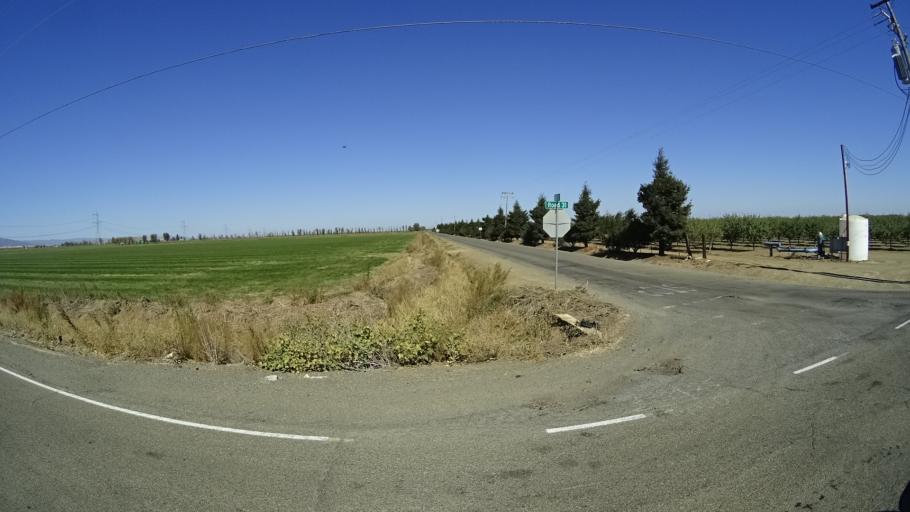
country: US
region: California
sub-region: Yolo County
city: Winters
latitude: 38.5618
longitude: -121.9053
